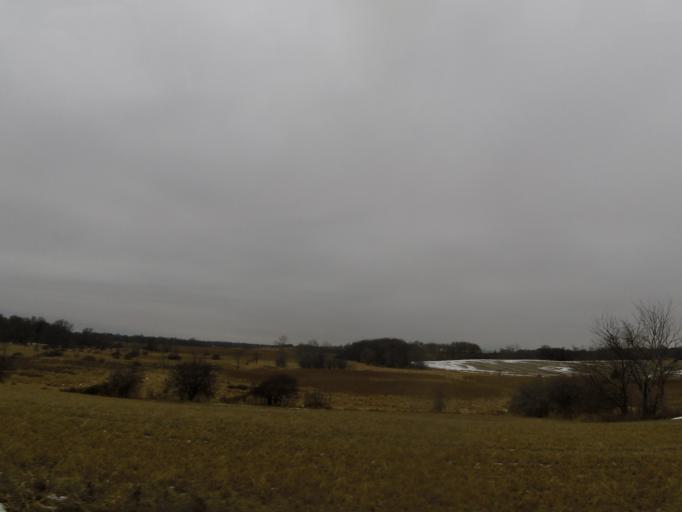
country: US
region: Minnesota
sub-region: Carver County
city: Watertown
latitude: 44.9887
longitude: -93.8489
